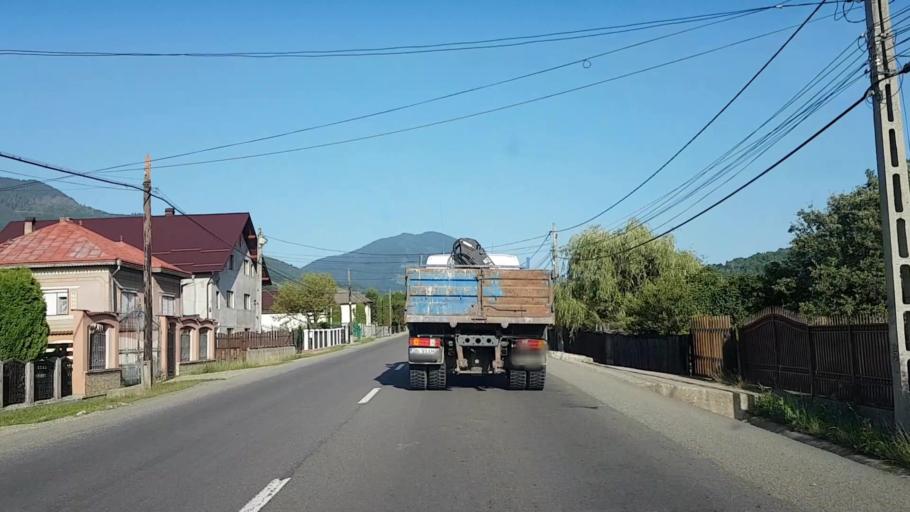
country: RO
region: Bistrita-Nasaud
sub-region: Comuna Tiha Bargaului
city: Tureac
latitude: 47.2266
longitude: 24.8102
